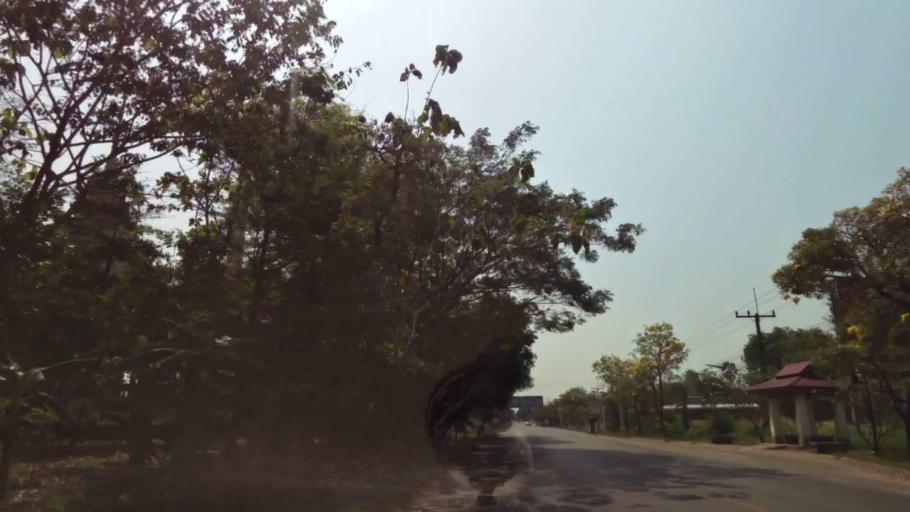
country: TH
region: Chanthaburi
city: Tha Mai
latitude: 12.5664
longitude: 101.9148
